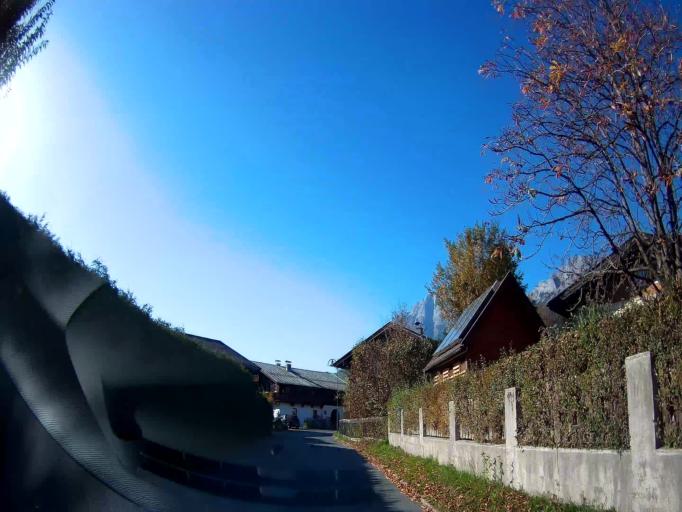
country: AT
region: Salzburg
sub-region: Politischer Bezirk Zell am See
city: Saalfelden am Steinernen Meer
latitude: 47.4459
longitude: 12.8170
